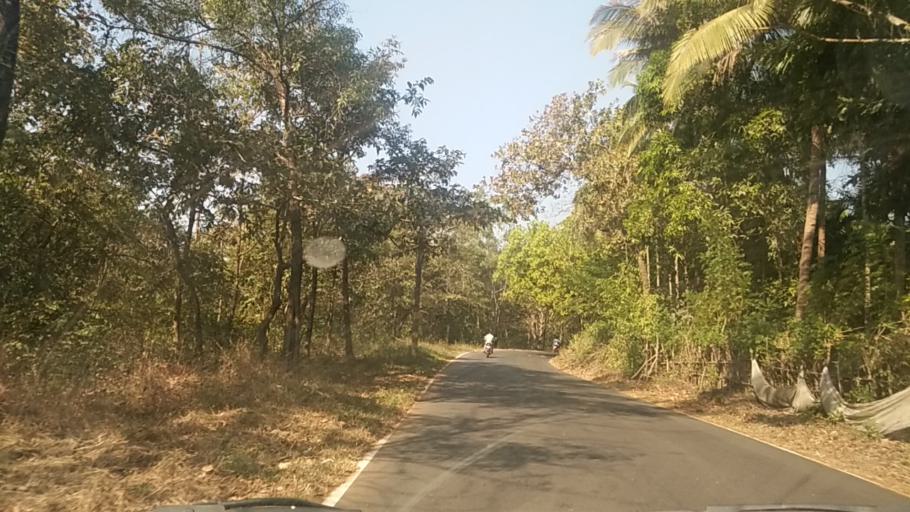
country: IN
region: Goa
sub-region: South Goa
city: Sanguem
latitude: 15.2069
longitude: 74.2204
